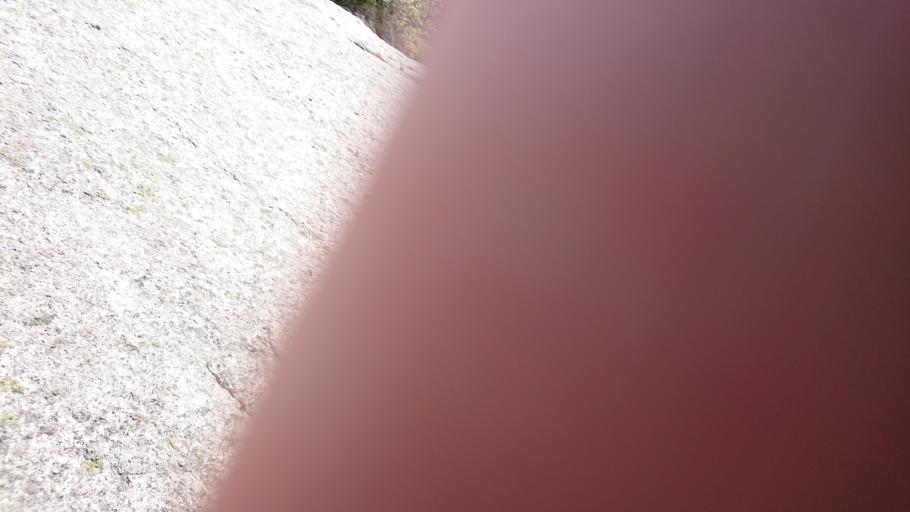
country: NO
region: Rogaland
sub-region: Sandnes
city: Sandnes
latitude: 58.9029
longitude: 5.7756
